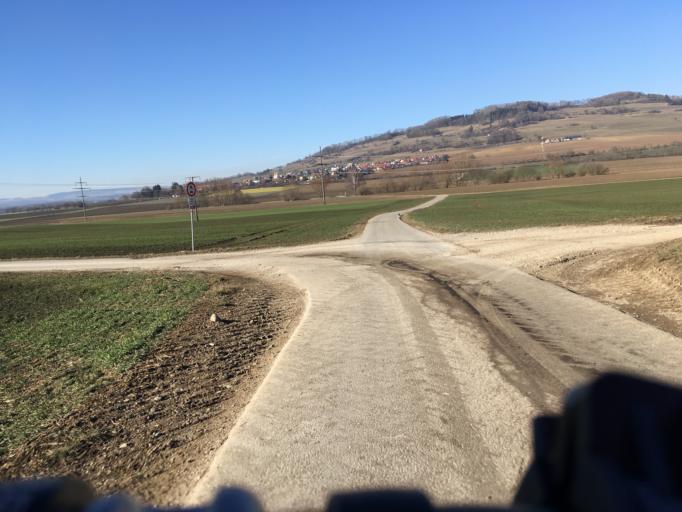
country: DE
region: Baden-Wuerttemberg
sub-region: Freiburg Region
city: Gottmadingen
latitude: 47.7537
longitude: 8.7581
